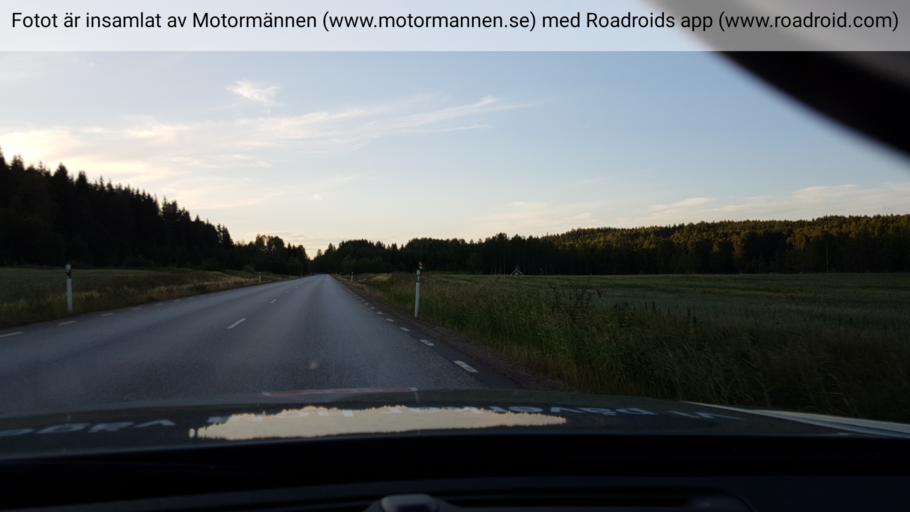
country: SE
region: Vaermland
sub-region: Storfors Kommun
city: Storfors
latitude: 59.5150
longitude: 14.3032
